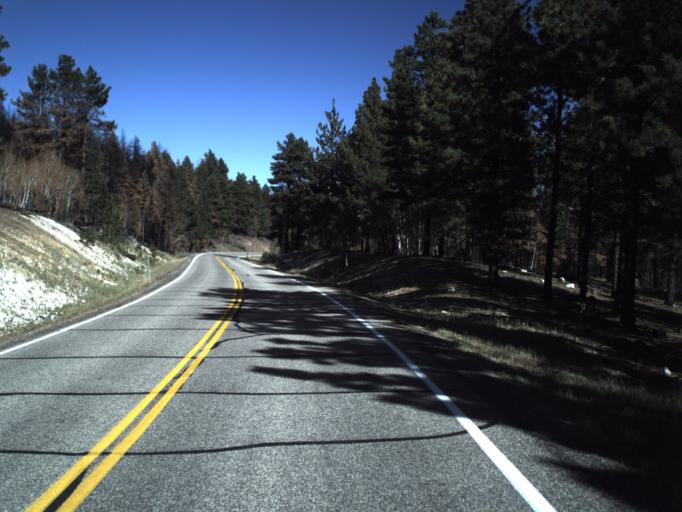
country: US
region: Utah
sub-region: Iron County
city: Parowan
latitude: 37.6547
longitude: -112.6809
